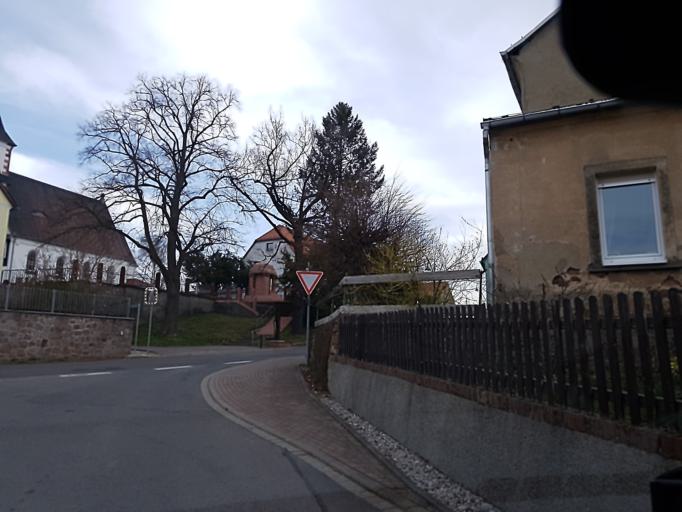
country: DE
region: Saxony
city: Grossweitzschen
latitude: 51.1574
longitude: 13.0450
